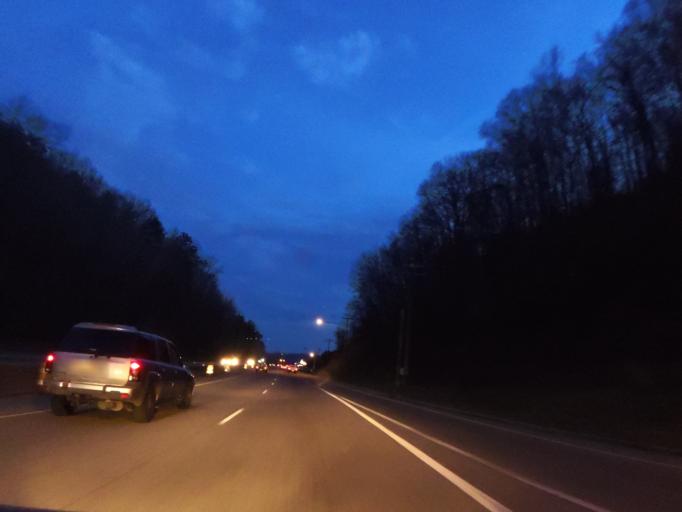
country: US
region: Tennessee
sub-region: Roane County
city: Oliver Springs
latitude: 36.0417
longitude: -84.3373
